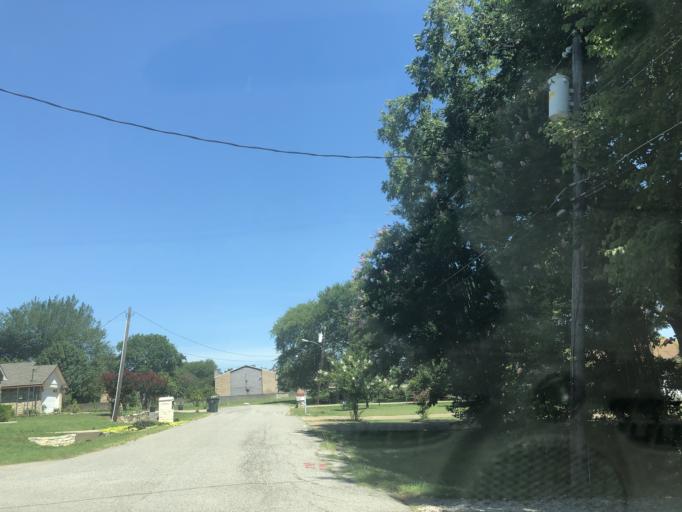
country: US
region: Texas
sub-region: Dallas County
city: Rowlett
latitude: 32.8502
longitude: -96.5962
